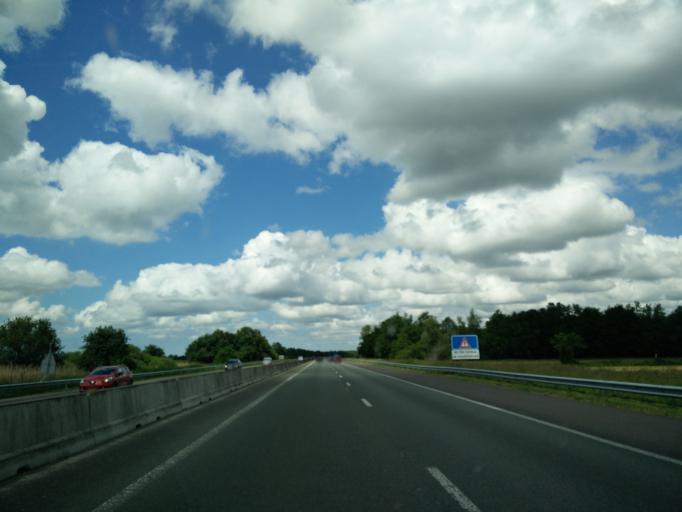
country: NL
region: Groningen
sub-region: Gemeente Haren
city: Haren
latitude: 53.1520
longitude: 6.6022
